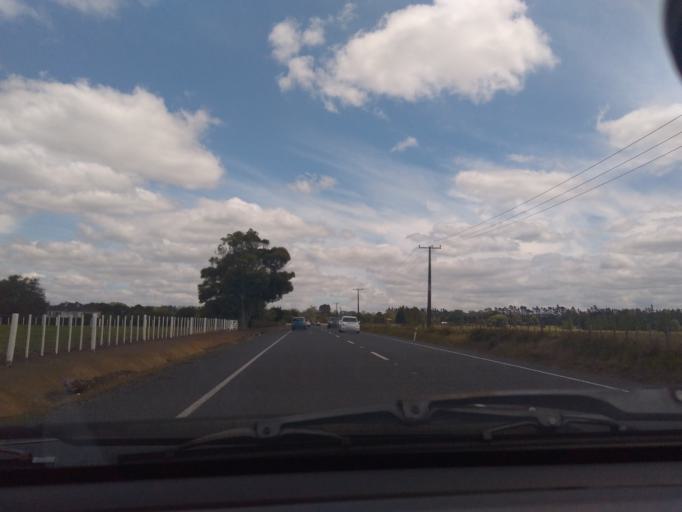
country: NZ
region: Northland
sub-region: Far North District
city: Kerikeri
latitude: -35.2268
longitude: 173.9204
